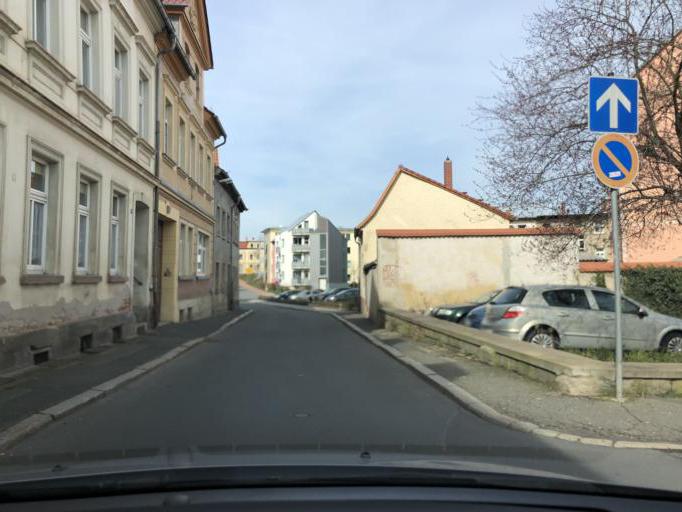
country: DE
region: Thuringia
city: Eisenberg
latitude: 50.9697
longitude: 11.9011
